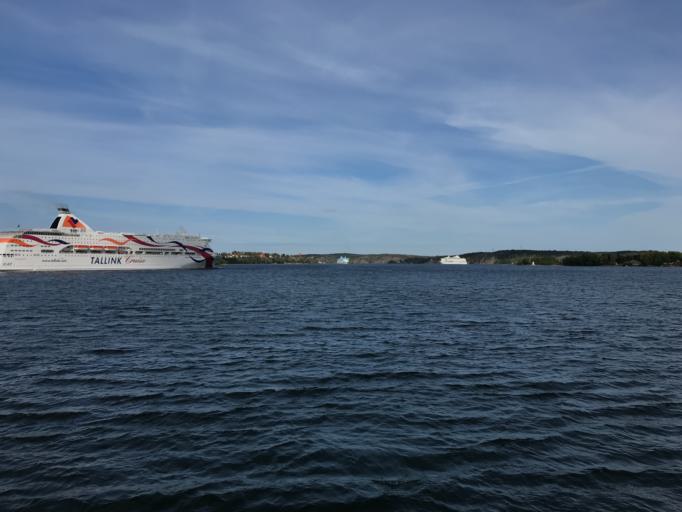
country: SE
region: Stockholm
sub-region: Nacka Kommun
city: Nacka
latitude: 59.3348
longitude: 18.1543
